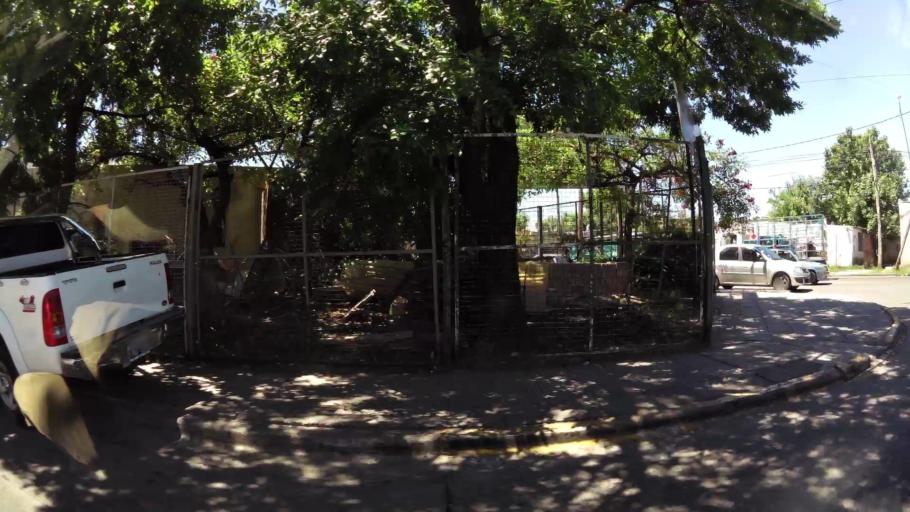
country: AR
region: Buenos Aires
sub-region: Partido de Tigre
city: Tigre
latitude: -34.4934
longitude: -58.5829
